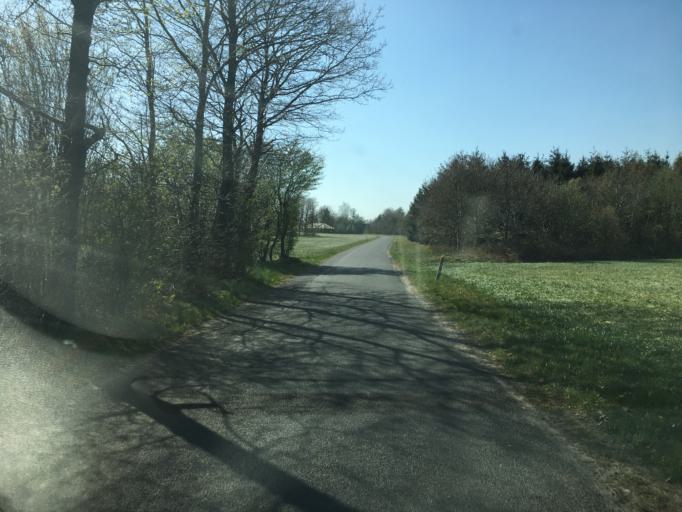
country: DK
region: South Denmark
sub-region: Aabenraa Kommune
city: Rodekro
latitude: 55.0966
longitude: 9.2661
